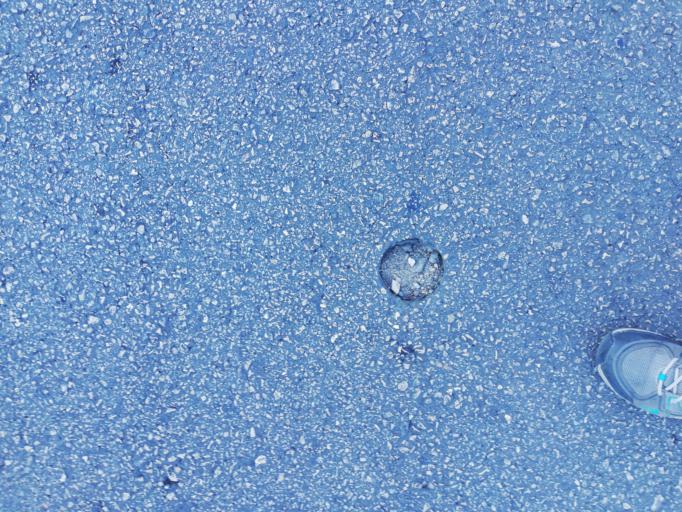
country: LB
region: Mont-Liban
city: Jdaidet el Matn
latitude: 33.8999
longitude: 35.5886
